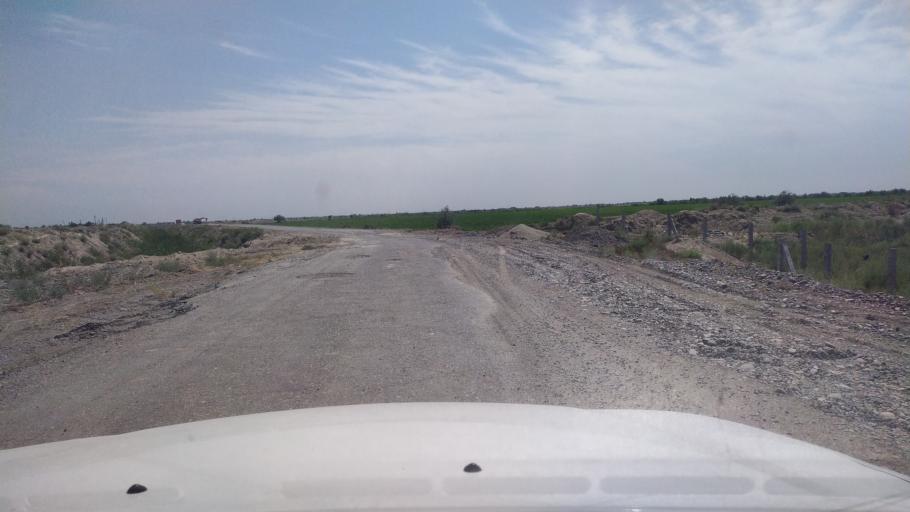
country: UZ
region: Namangan
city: Toshbuloq
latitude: 40.7895
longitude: 71.5627
